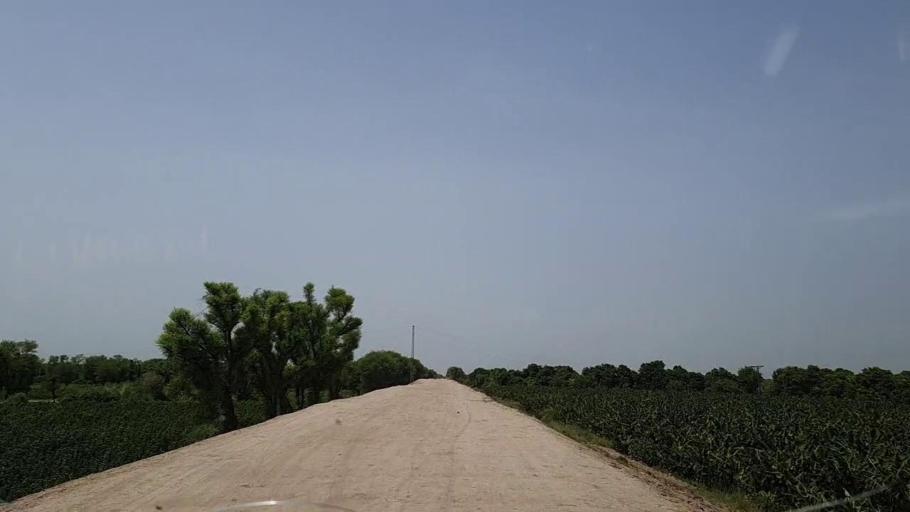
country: PK
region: Sindh
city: Tharu Shah
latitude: 27.0253
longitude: 68.1167
